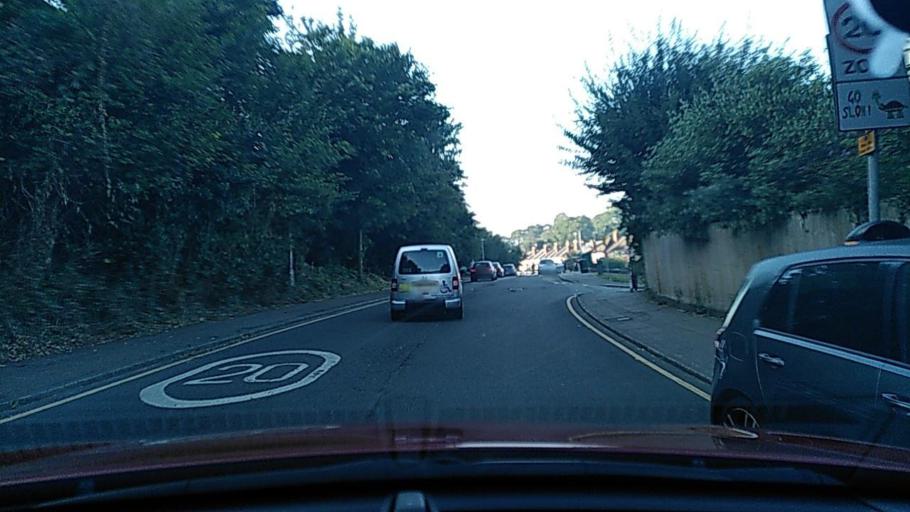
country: GB
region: England
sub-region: Reading
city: Reading
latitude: 51.4743
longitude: -0.9742
